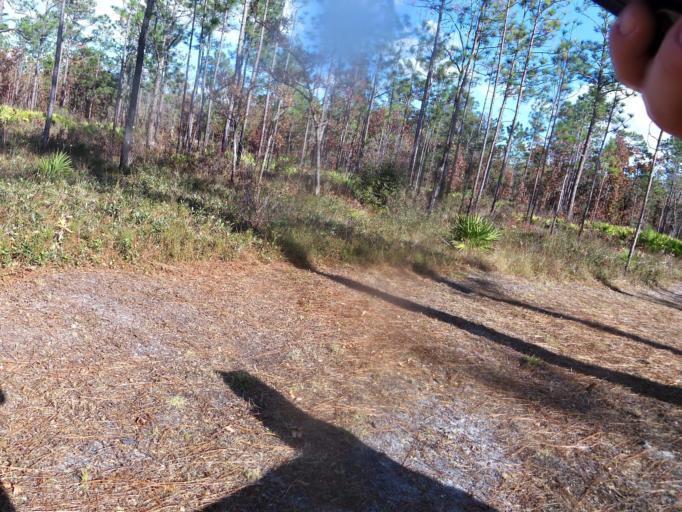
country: US
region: Florida
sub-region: Clay County
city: Middleburg
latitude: 30.1388
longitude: -81.9591
